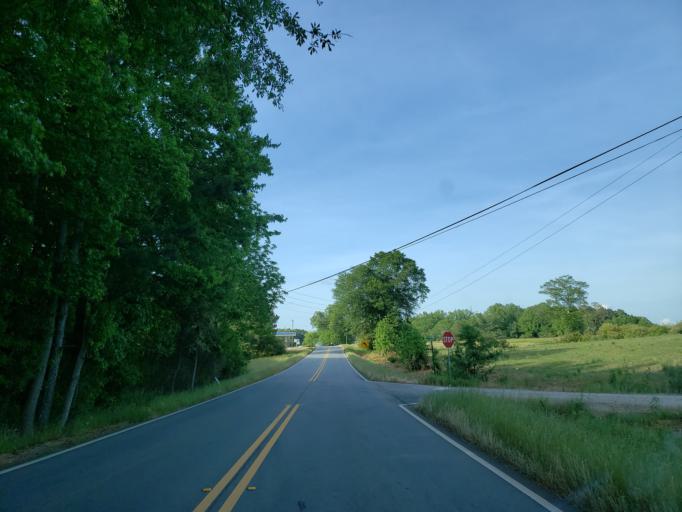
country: US
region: Georgia
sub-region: Carroll County
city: Bowdon
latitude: 33.4844
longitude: -85.2849
